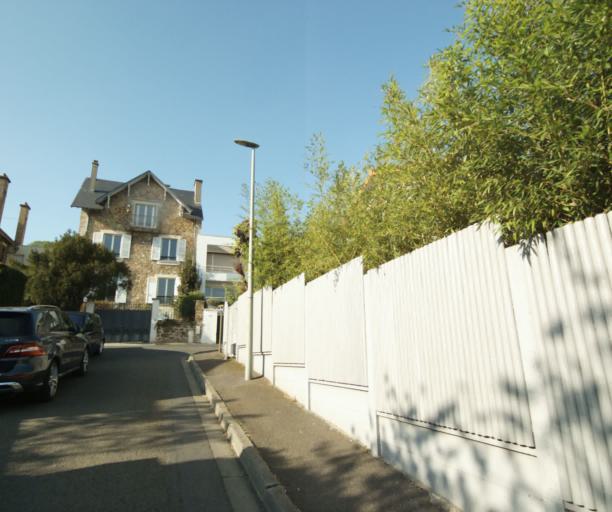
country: FR
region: Ile-de-France
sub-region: Departement des Hauts-de-Seine
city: Sevres
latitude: 48.8268
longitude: 2.2113
